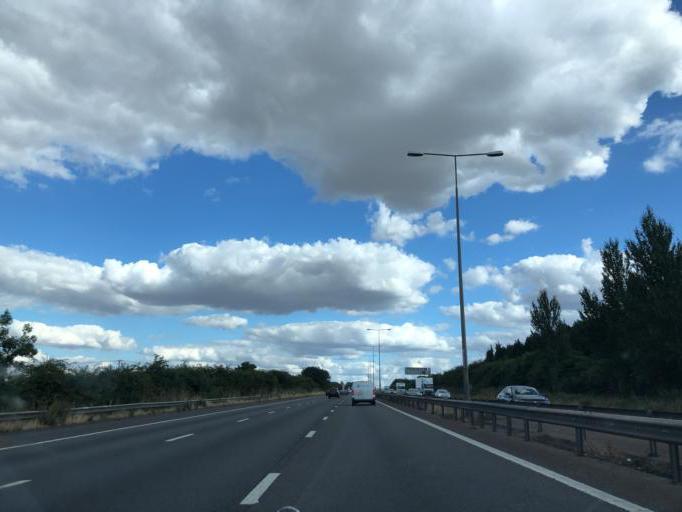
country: GB
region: England
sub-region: Northamptonshire
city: Roade
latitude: 52.1729
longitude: -0.8718
